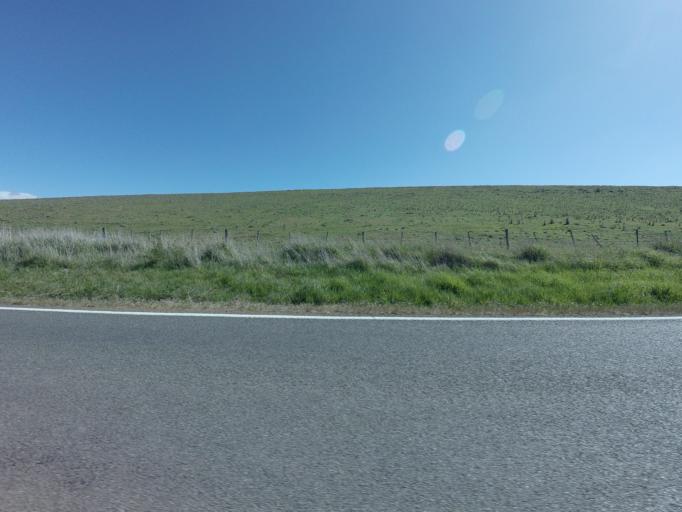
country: AU
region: Tasmania
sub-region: Derwent Valley
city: New Norfolk
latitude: -42.6390
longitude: 146.9181
